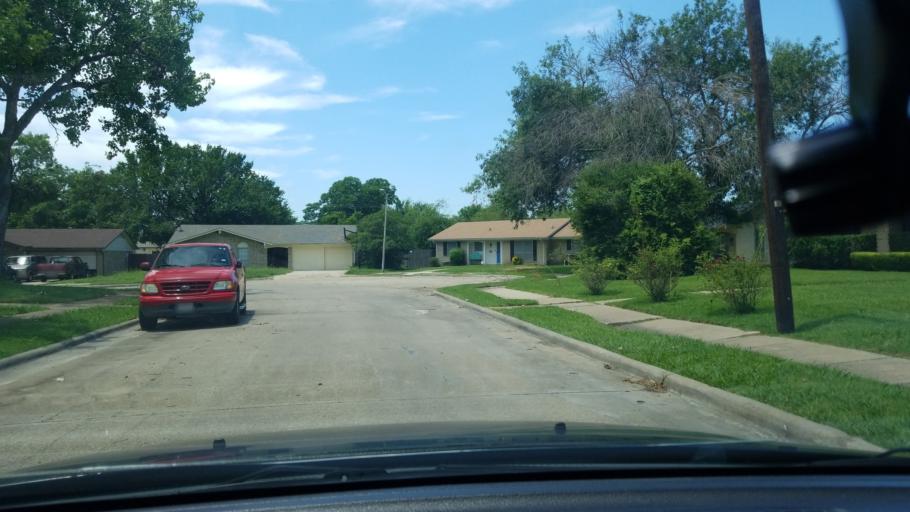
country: US
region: Texas
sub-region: Dallas County
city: Mesquite
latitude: 32.8088
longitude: -96.6520
